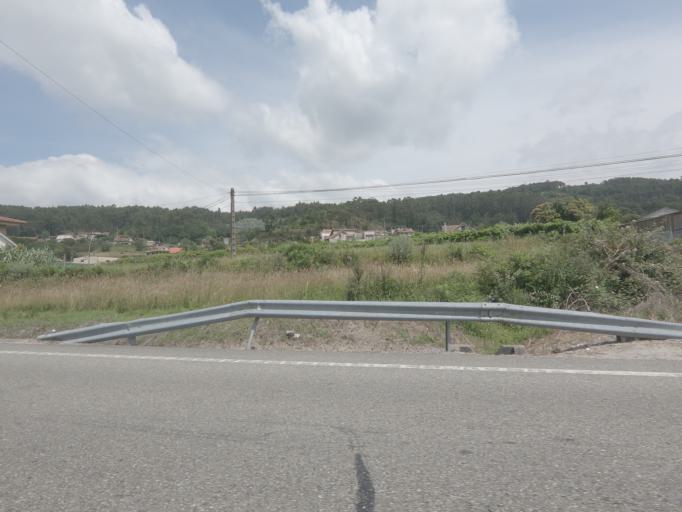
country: ES
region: Galicia
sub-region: Provincia de Pontevedra
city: Tomino
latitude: 42.0346
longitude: -8.7291
